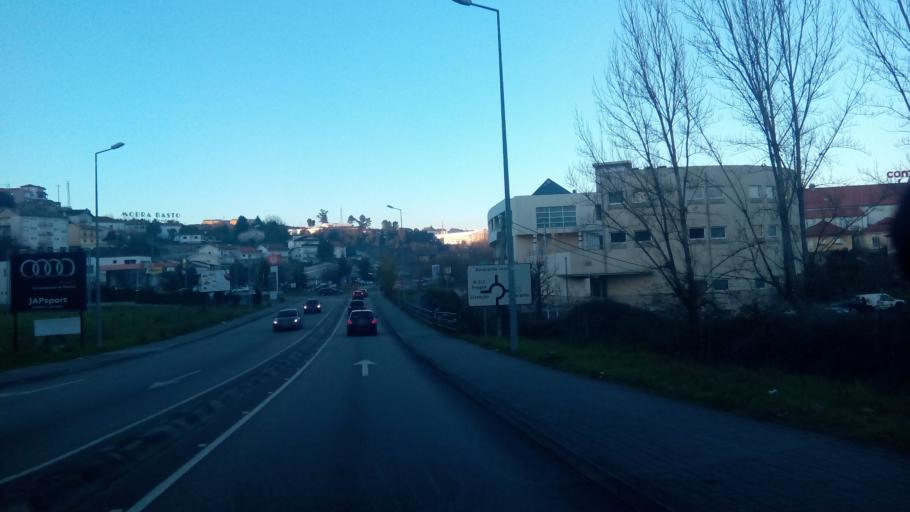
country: PT
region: Porto
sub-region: Amarante
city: Amarante
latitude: 41.2714
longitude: -8.0890
